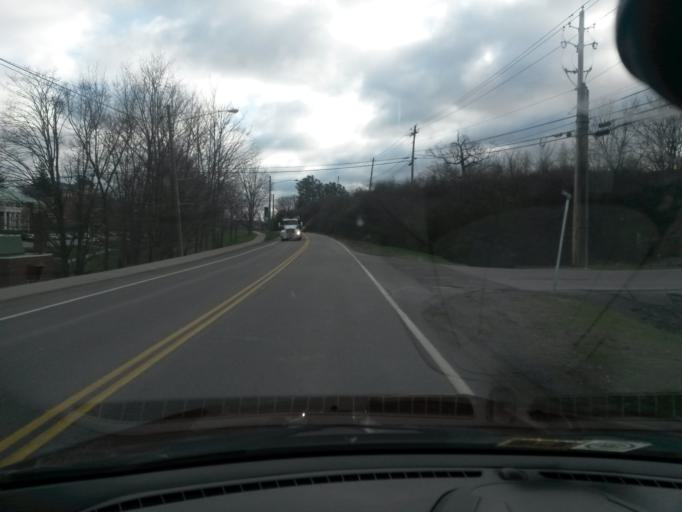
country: US
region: Virginia
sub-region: Tazewell County
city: Bluefield
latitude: 37.2422
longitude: -81.2485
